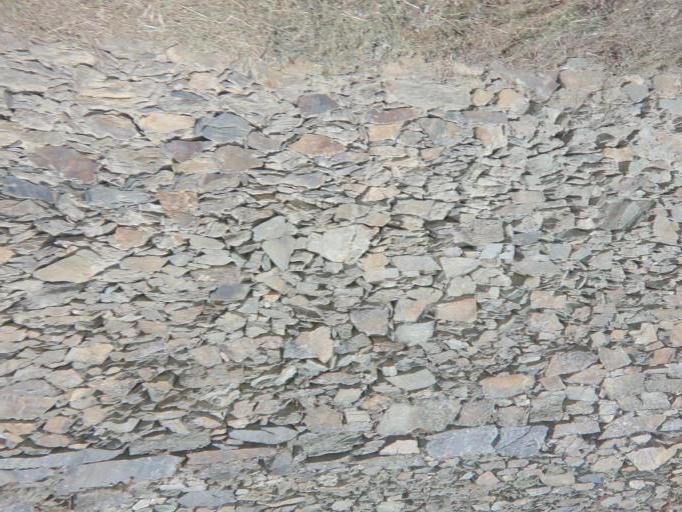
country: PT
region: Vila Real
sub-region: Sabrosa
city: Vilela
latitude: 41.2057
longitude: -7.5523
